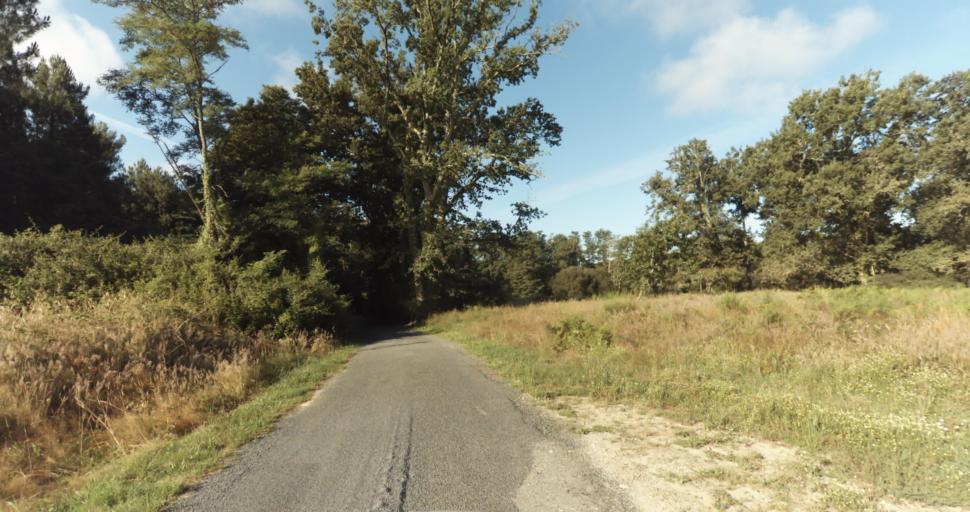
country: FR
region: Aquitaine
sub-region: Departement de la Gironde
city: Bazas
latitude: 44.4510
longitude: -0.2527
